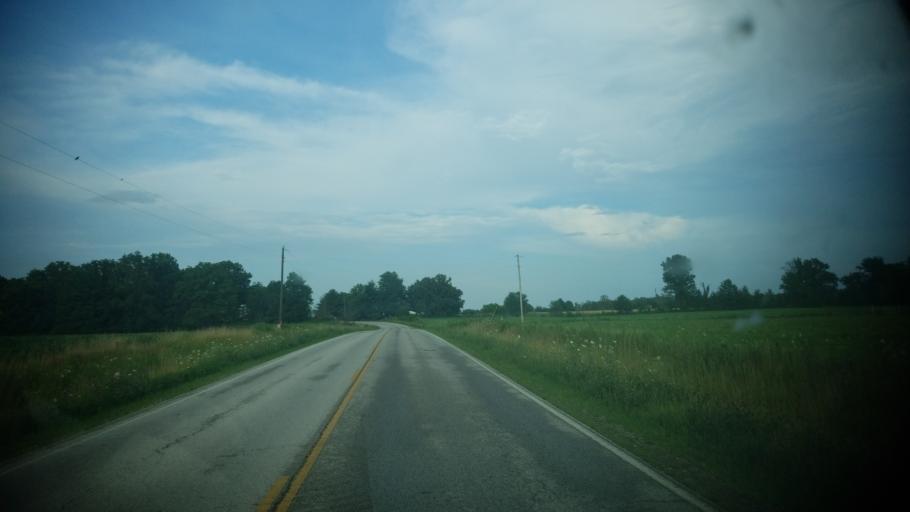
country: US
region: Illinois
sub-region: Clay County
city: Flora
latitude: 38.5167
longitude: -88.4882
